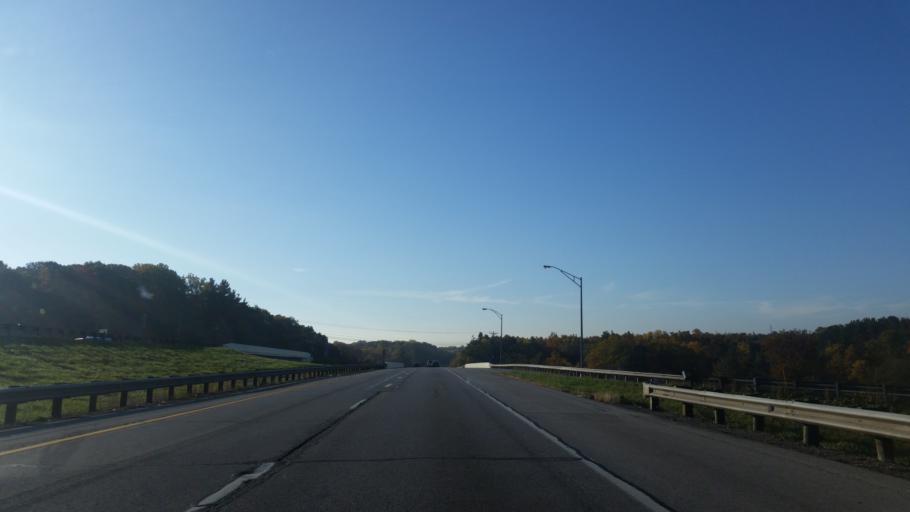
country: US
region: Ohio
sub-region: Summit County
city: Richfield
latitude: 41.2601
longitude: -81.6336
